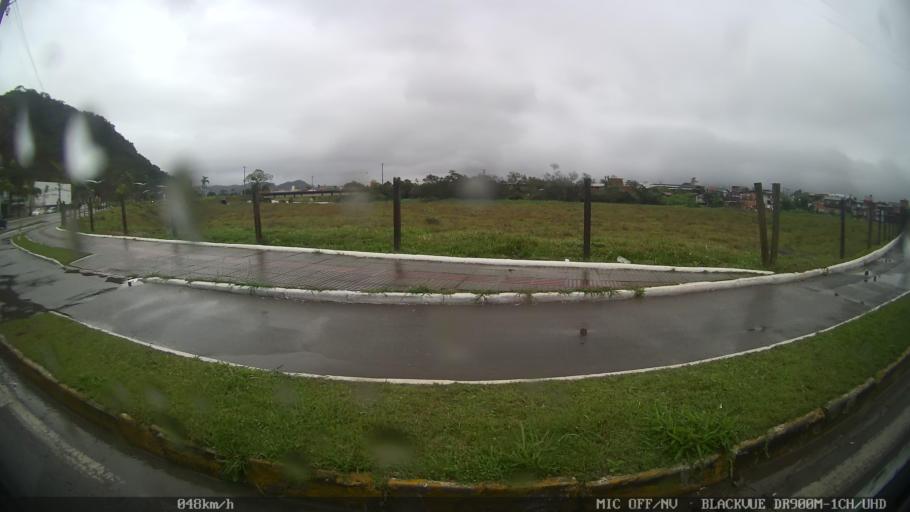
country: BR
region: Santa Catarina
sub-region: Itajai
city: Itajai
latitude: -26.9330
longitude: -48.6903
